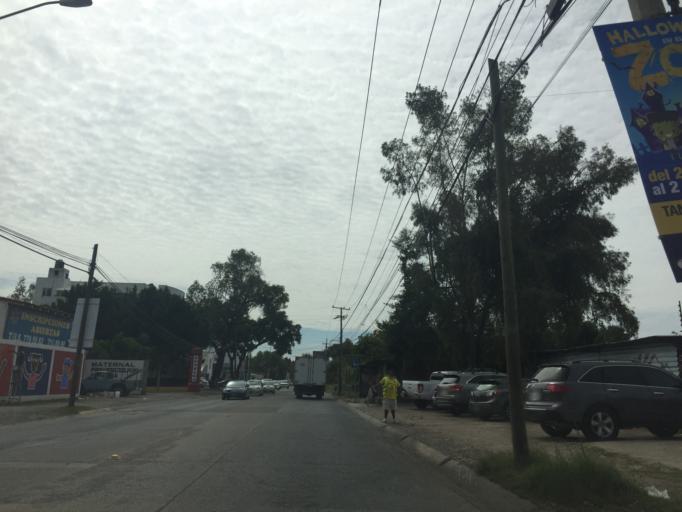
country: MX
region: Guanajuato
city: Leon
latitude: 21.1649
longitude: -101.6845
